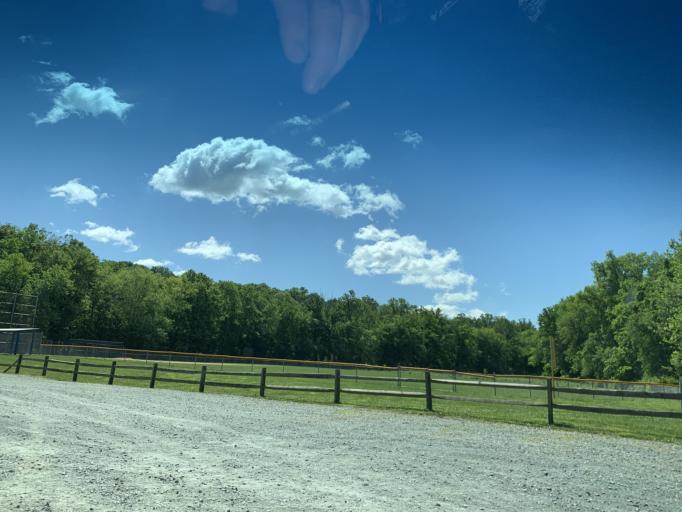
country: US
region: Maryland
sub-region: Cecil County
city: Rising Sun
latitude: 39.6554
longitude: -76.1556
